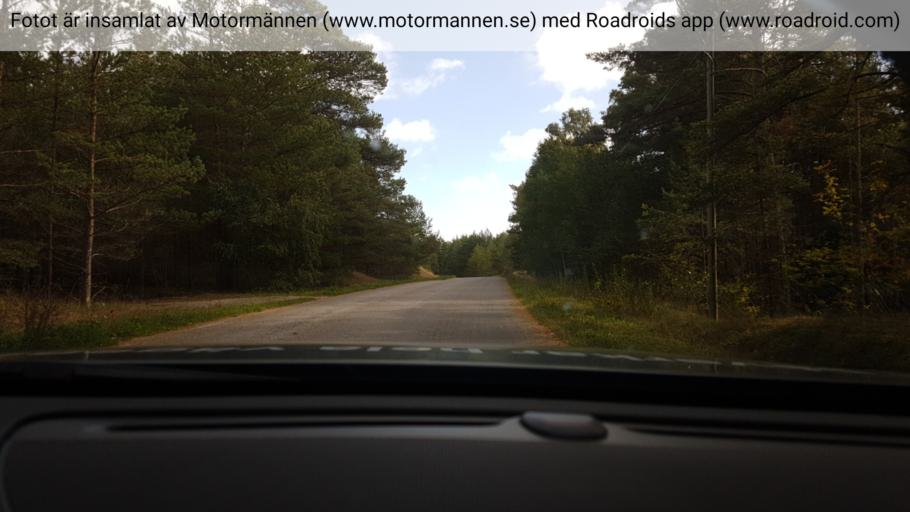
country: SE
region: Gotland
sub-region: Gotland
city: Slite
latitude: 57.9553
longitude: 19.2807
